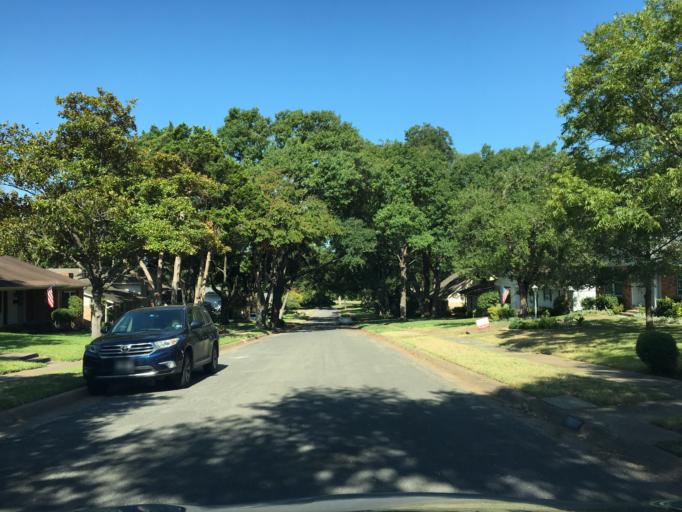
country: US
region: Texas
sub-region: Dallas County
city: Garland
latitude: 32.8567
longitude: -96.6932
